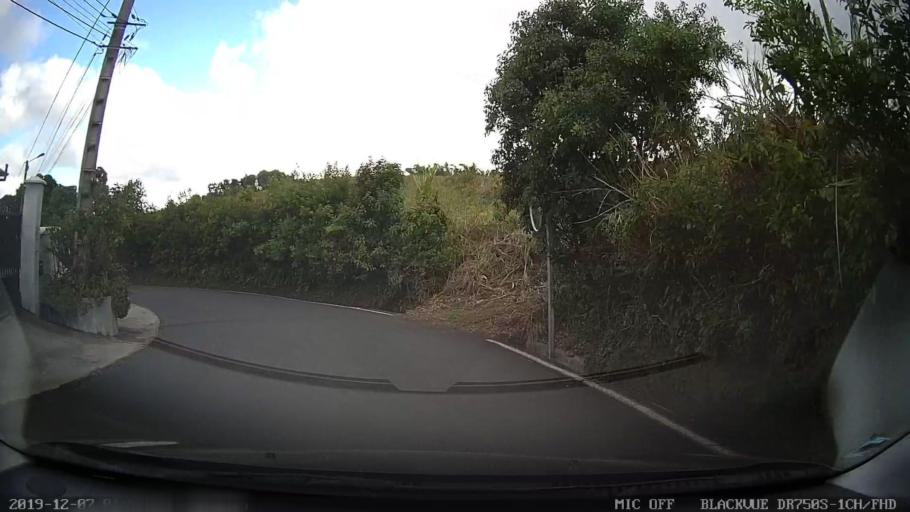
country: RE
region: Reunion
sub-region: Reunion
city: Sainte-Marie
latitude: -20.9381
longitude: 55.5336
